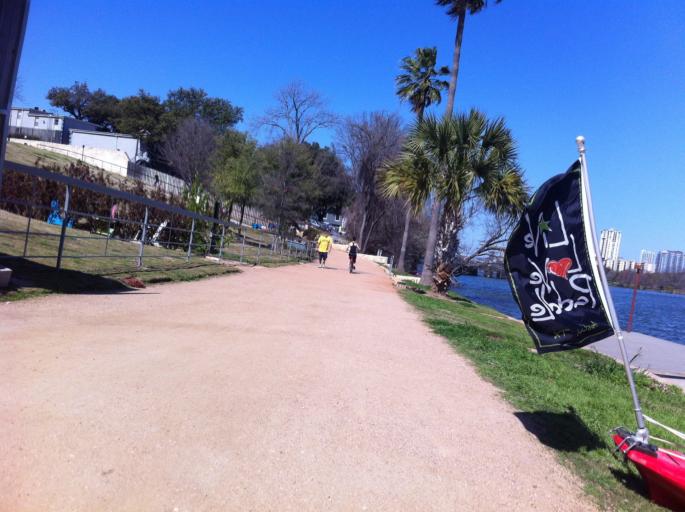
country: US
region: Texas
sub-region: Travis County
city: Austin
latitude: 30.2460
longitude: -97.7274
